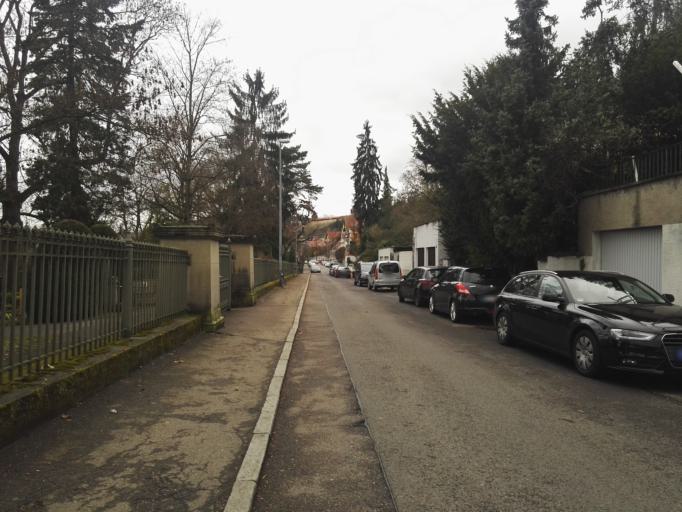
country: DE
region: Baden-Wuerttemberg
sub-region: Regierungsbezirk Stuttgart
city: Esslingen
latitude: 48.7409
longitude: 9.3196
